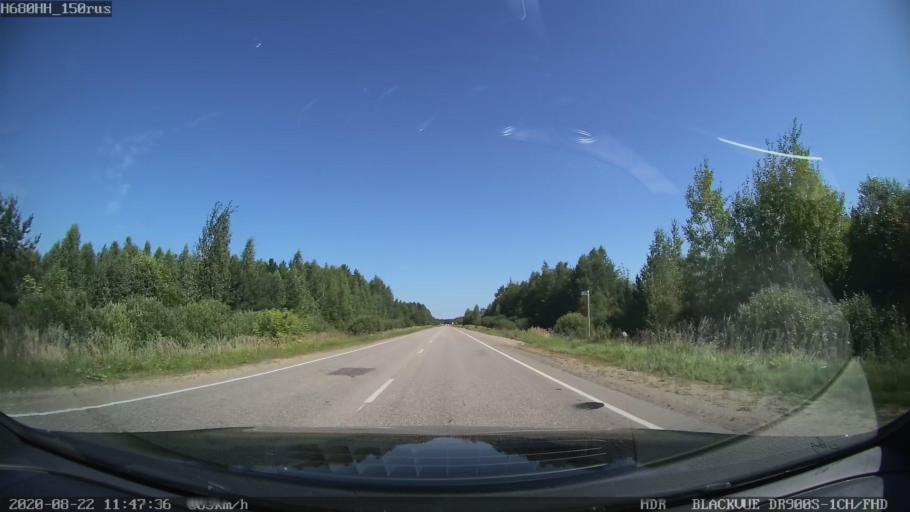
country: RU
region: Tverskaya
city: Sakharovo
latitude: 57.0542
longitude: 36.0897
